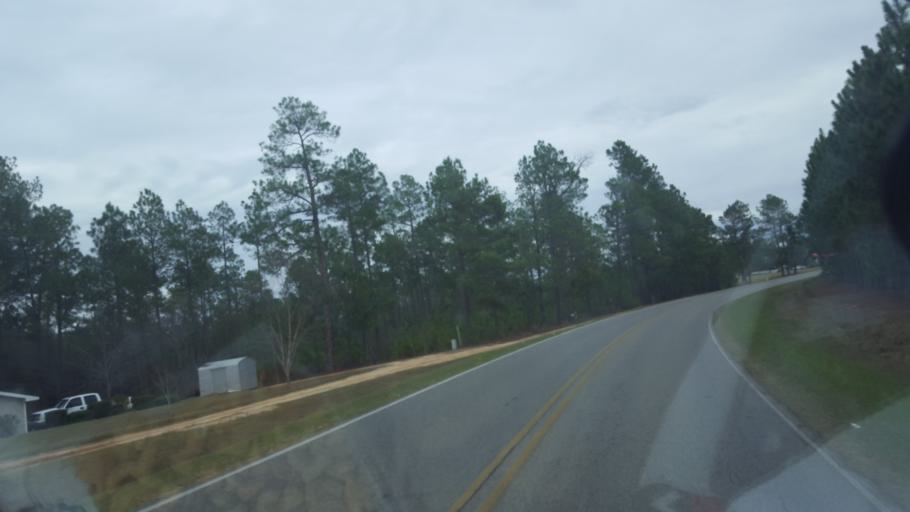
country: US
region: Georgia
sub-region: Ben Hill County
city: Fitzgerald
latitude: 31.7563
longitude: -83.3399
